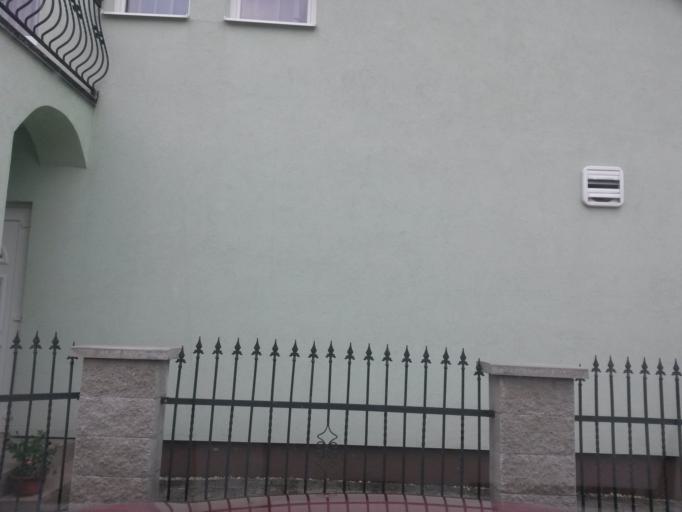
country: SK
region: Kosicky
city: Spisska Nova Ves
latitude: 48.8479
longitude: 20.6119
